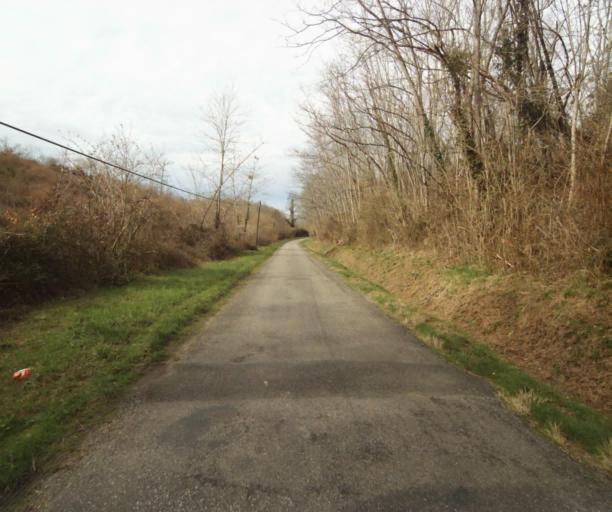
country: FR
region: Aquitaine
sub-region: Departement des Landes
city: Gabarret
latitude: 43.9803
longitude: 0.0219
